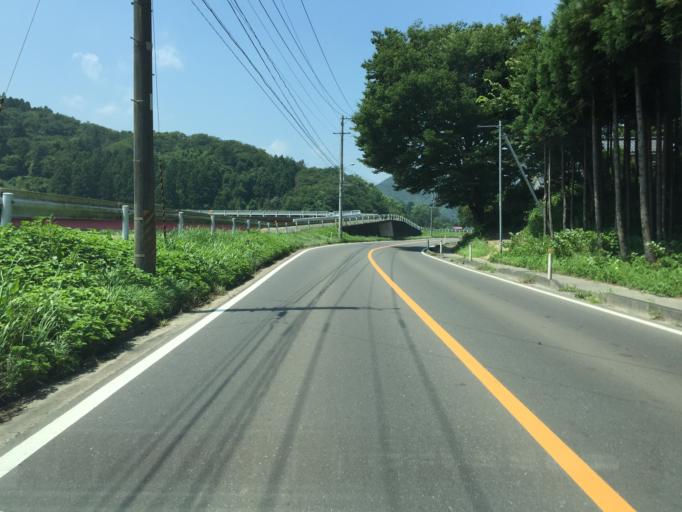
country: JP
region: Miyagi
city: Marumori
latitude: 37.8918
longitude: 140.8054
